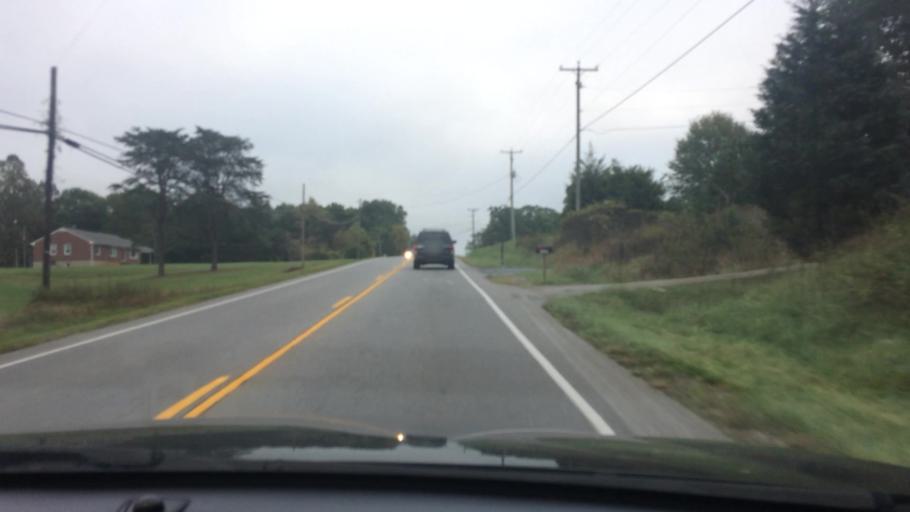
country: US
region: Virginia
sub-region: Franklin County
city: Rocky Mount
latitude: 37.0177
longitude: -79.8360
